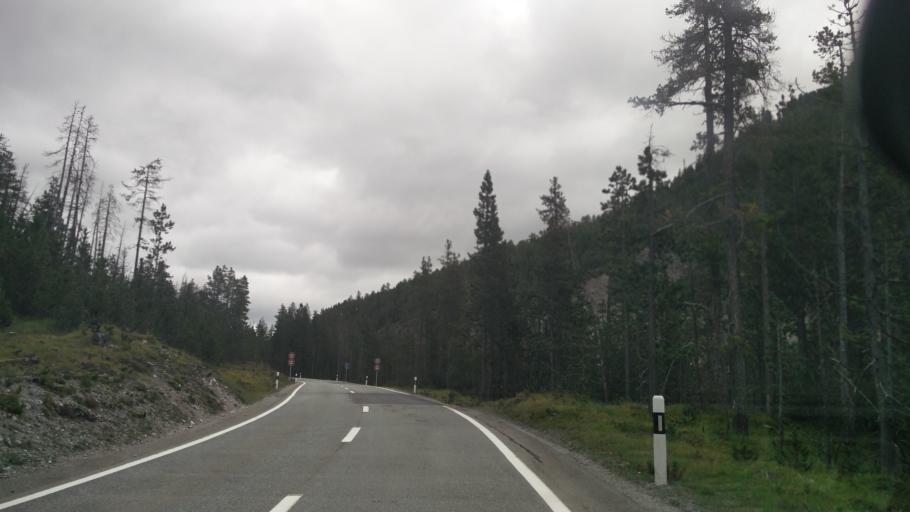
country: CH
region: Grisons
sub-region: Inn District
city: Zernez
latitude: 46.6622
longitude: 10.2210
